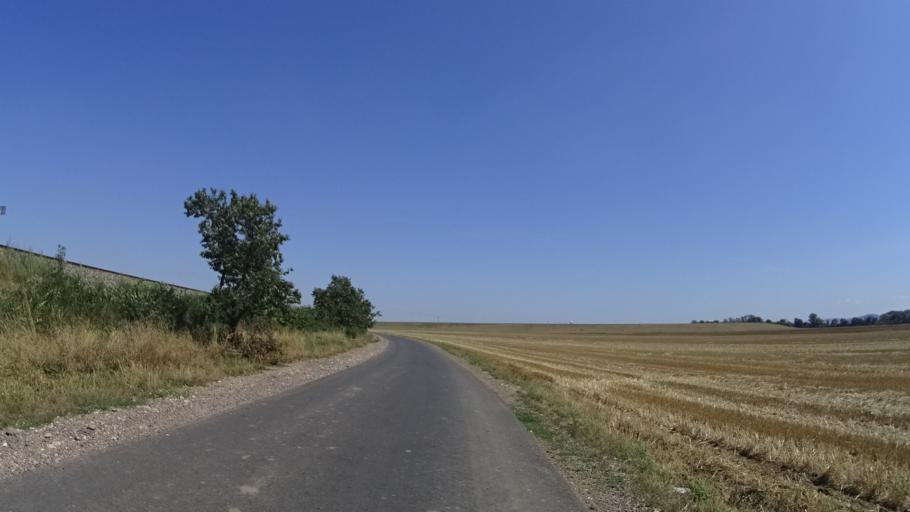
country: CZ
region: South Moravian
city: Petrov
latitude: 48.8801
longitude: 17.2816
